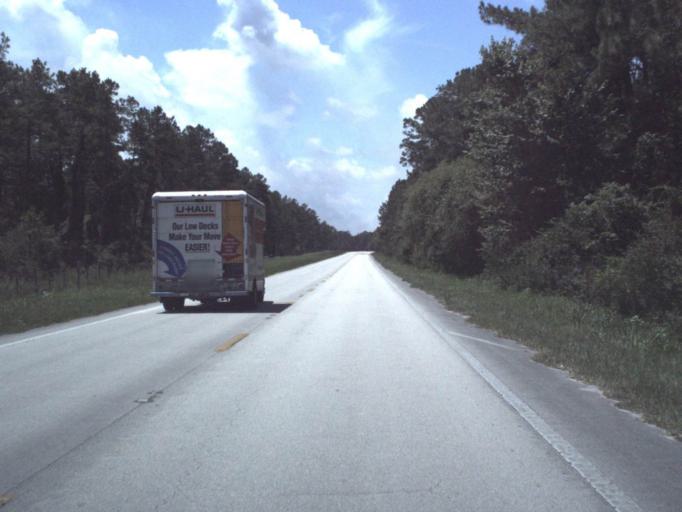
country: US
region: Florida
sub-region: Bradford County
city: Starke
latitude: 29.9483
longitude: -82.0163
